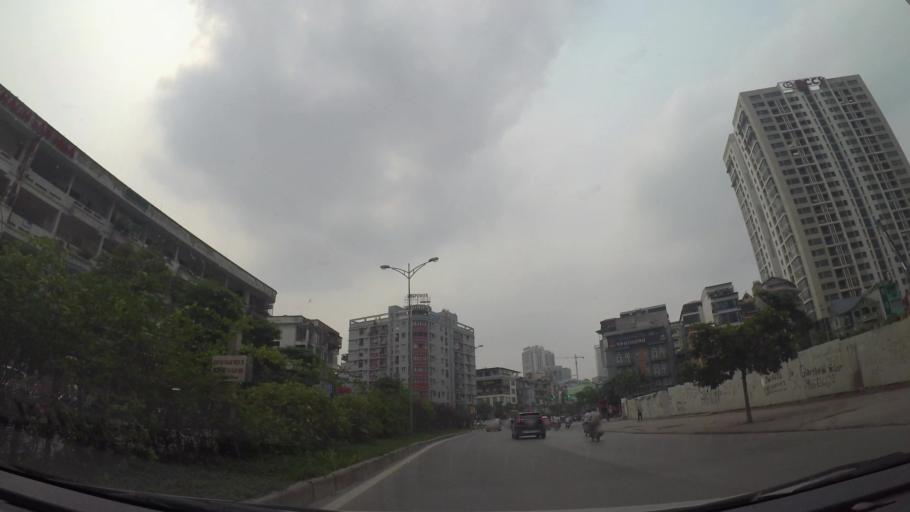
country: VN
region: Ha Noi
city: Cau Dien
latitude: 21.0295
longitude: 105.7760
